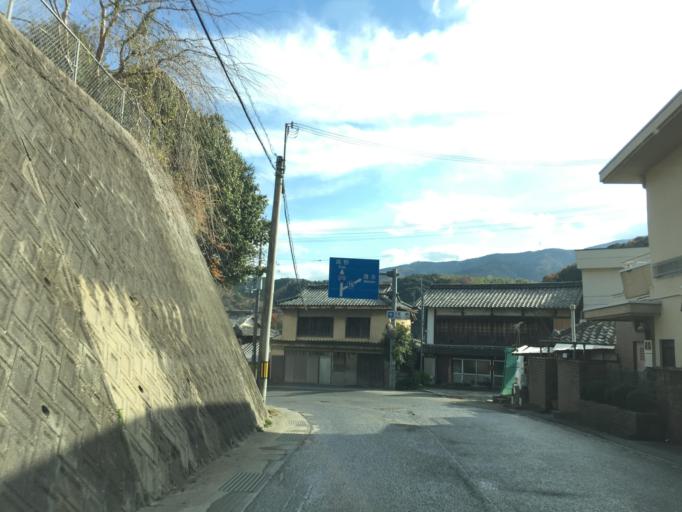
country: JP
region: Wakayama
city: Iwade
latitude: 34.1490
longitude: 135.3574
